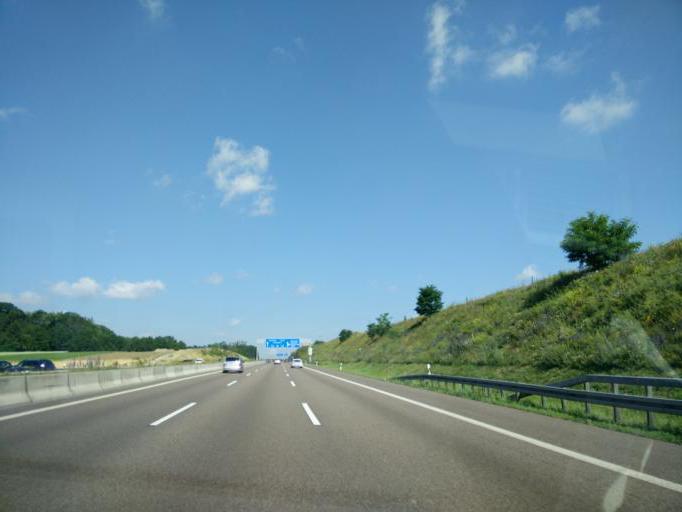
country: DE
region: Baden-Wuerttemberg
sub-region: Regierungsbezirk Stuttgart
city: Rutesheim
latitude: 48.8049
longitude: 8.9328
